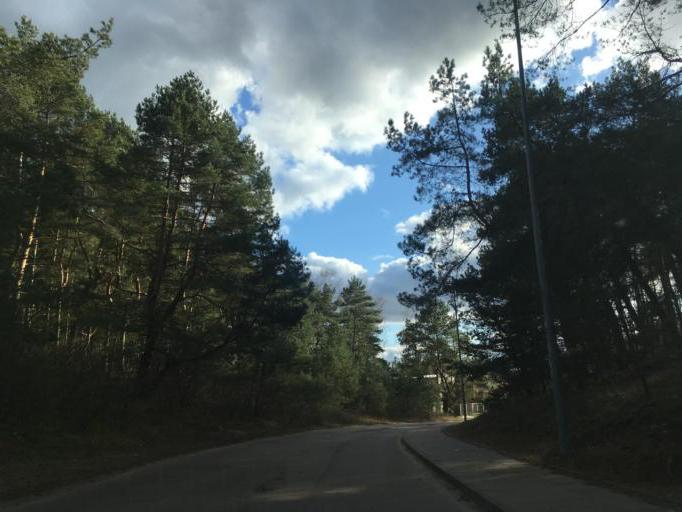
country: PL
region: Pomeranian Voivodeship
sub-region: Powiat gdanski
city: Cedry Wielkie
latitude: 54.3460
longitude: 18.8354
